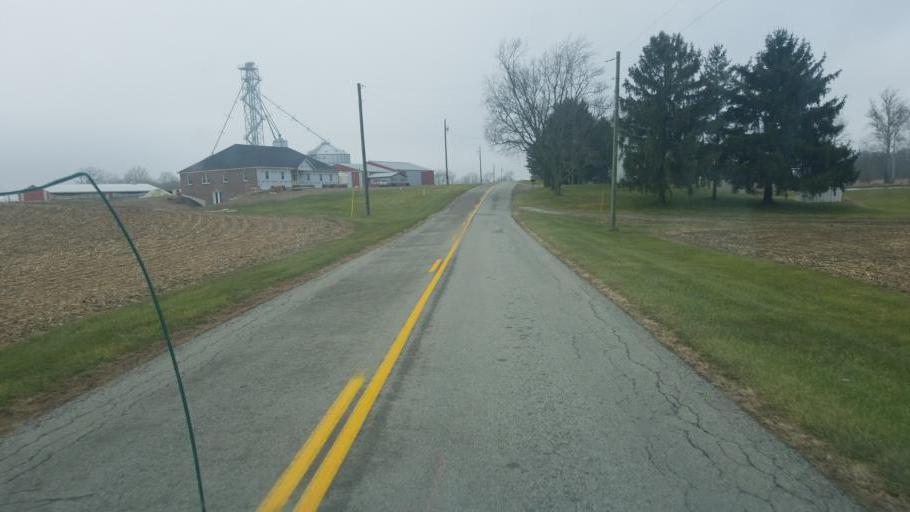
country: US
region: Ohio
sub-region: Champaign County
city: North Lewisburg
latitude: 40.2516
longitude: -83.5416
